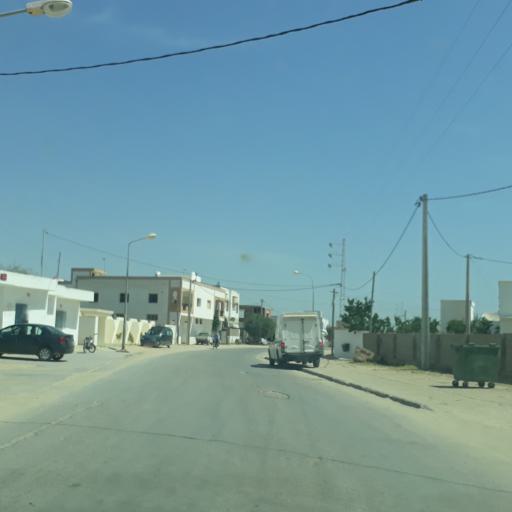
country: TN
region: Safaqis
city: Al Qarmadah
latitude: 34.8189
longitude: 10.7770
